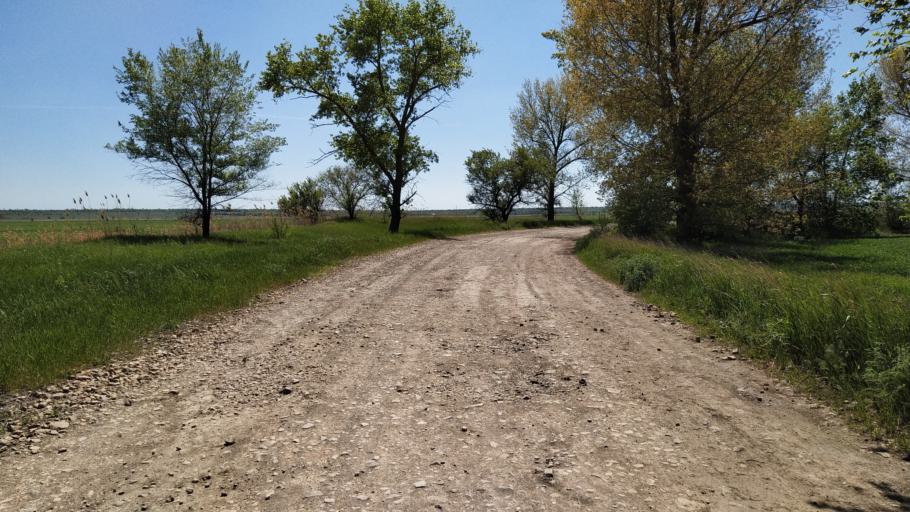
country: RU
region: Rostov
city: Kuleshovka
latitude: 47.0578
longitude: 39.6252
